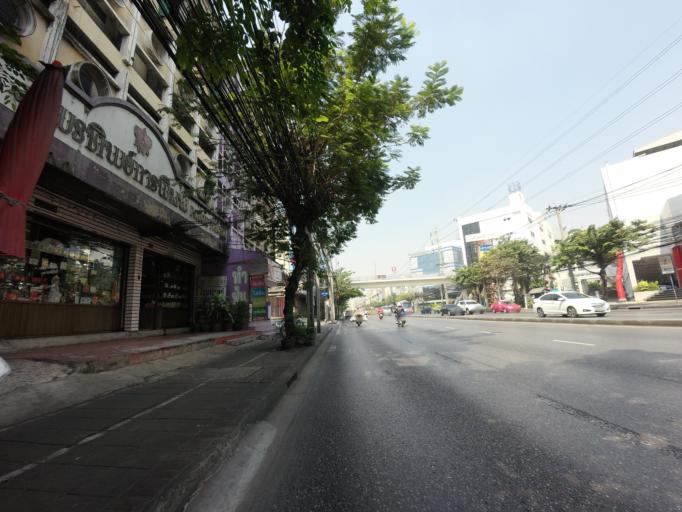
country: TH
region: Bangkok
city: Bang Kapi
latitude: 13.7728
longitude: 100.6329
